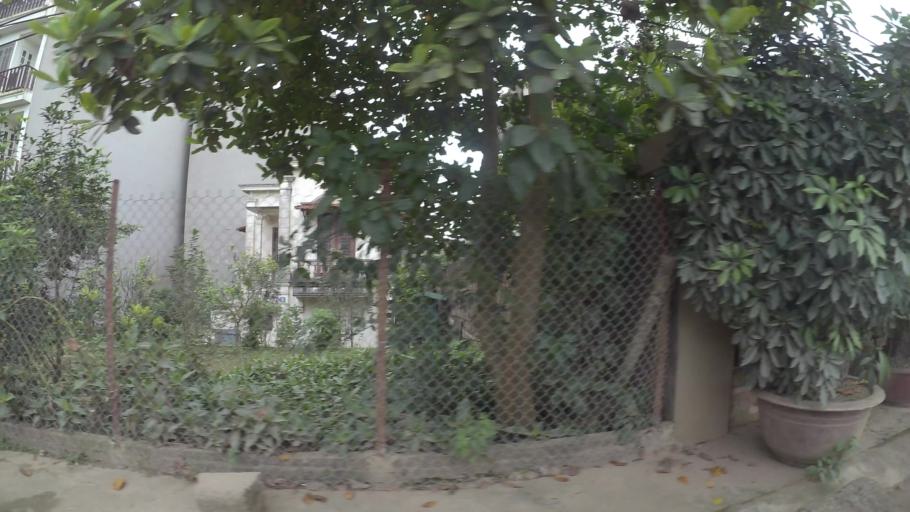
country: VN
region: Ha Noi
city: Tay Ho
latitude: 21.0745
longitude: 105.8267
